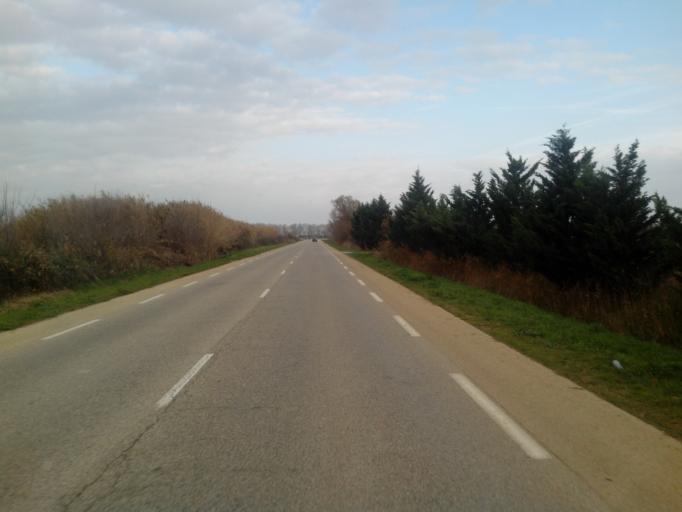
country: FR
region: Languedoc-Roussillon
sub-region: Departement du Gard
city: Saint-Gilles
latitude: 43.5780
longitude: 4.4332
